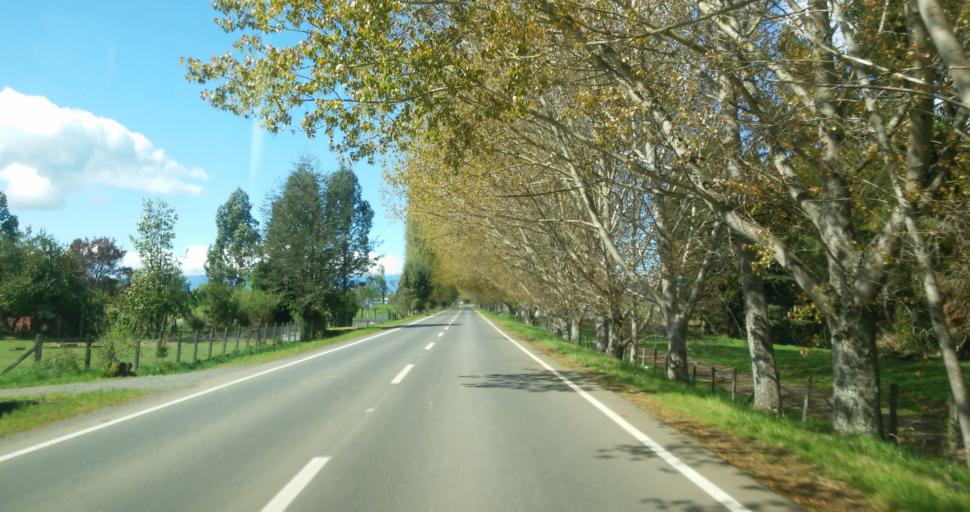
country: CL
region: Los Rios
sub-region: Provincia del Ranco
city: Rio Bueno
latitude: -40.2432
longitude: -72.6141
